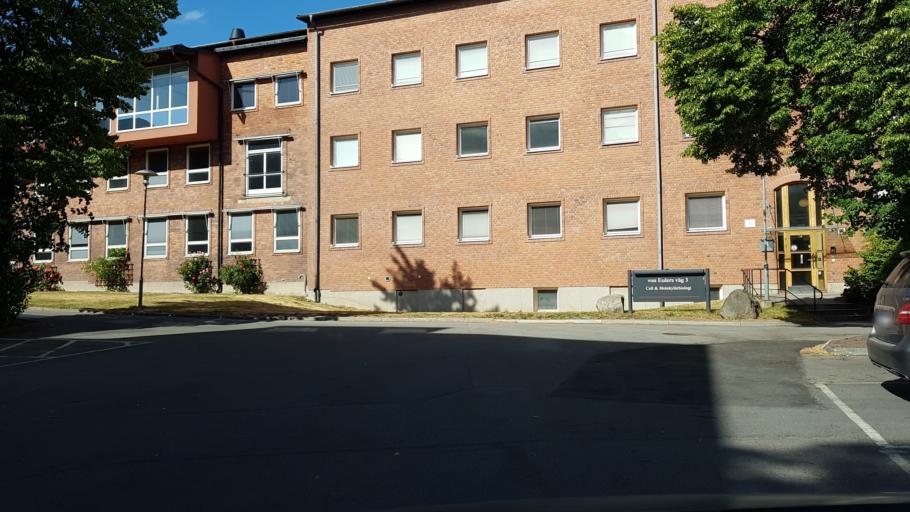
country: SE
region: Stockholm
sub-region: Solna Kommun
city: Solna
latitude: 59.3465
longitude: 18.0277
